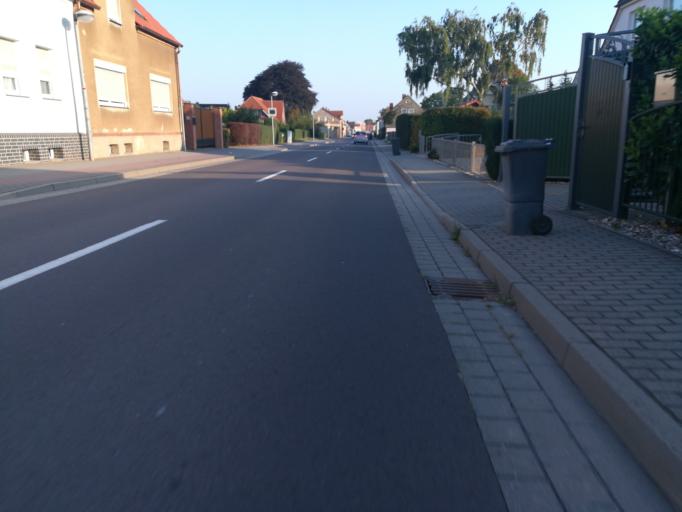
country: DE
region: Saxony-Anhalt
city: Irxleben
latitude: 52.1624
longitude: 11.4845
